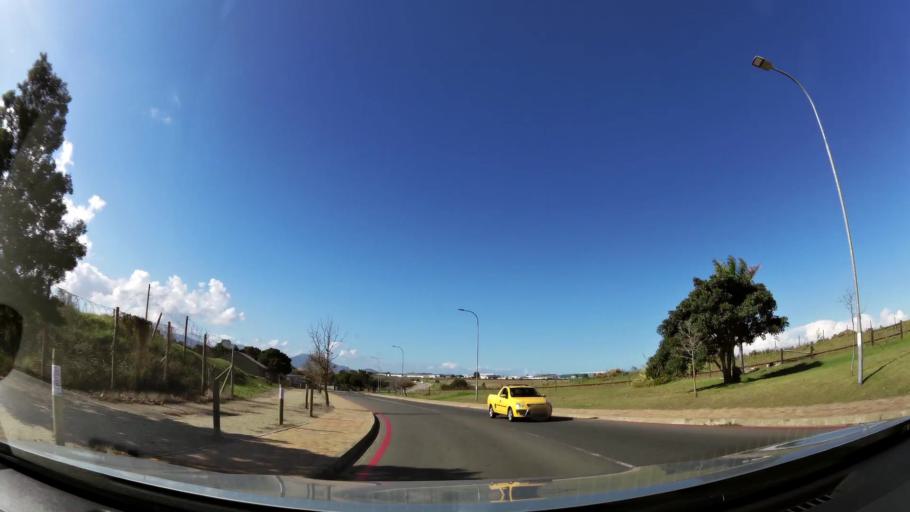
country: ZA
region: Western Cape
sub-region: Eden District Municipality
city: George
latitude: -33.9822
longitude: 22.4434
